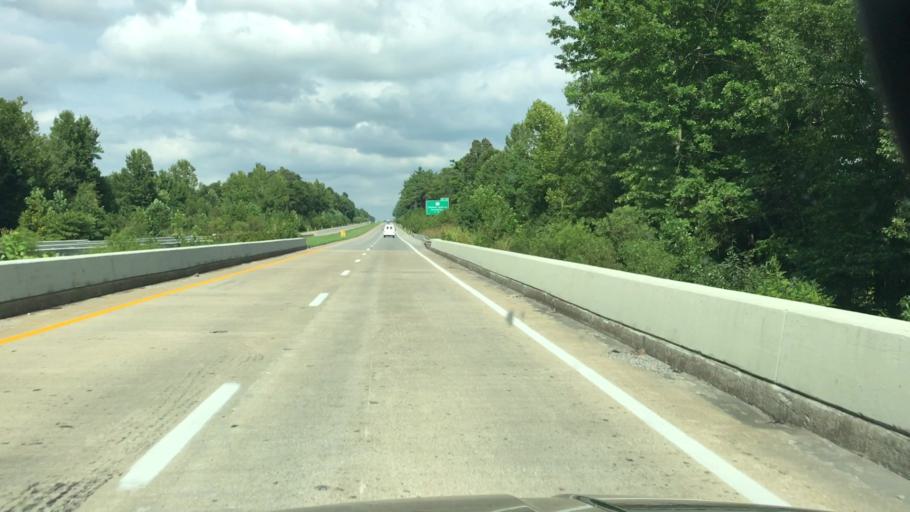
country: US
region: Kentucky
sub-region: Hopkins County
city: Dawson Springs
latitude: 37.1808
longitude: -87.7273
